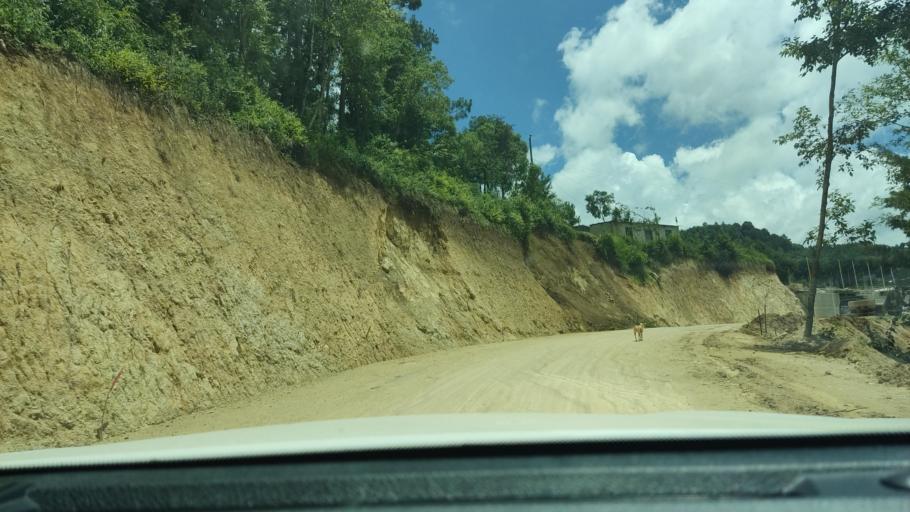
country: GT
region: Chimaltenango
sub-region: Municipio de San Juan Comalapa
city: Comalapa
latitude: 14.7802
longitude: -90.8691
